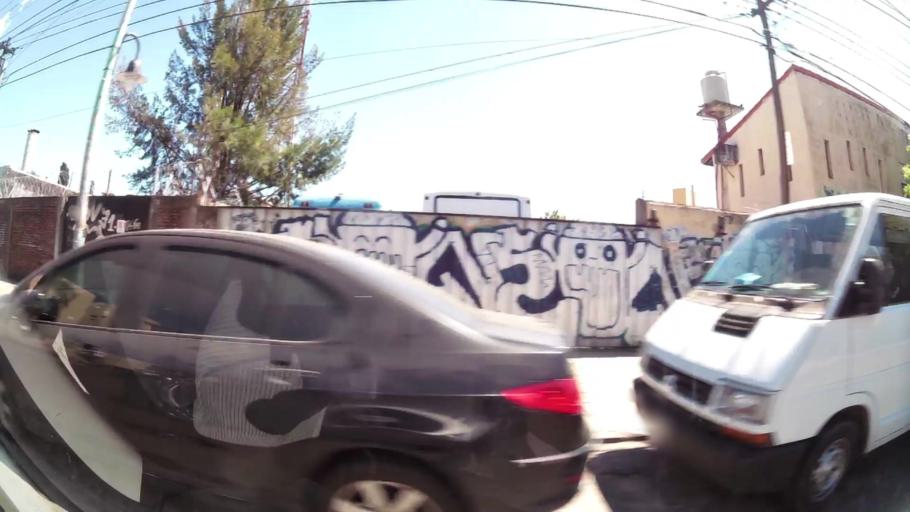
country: AR
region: Buenos Aires
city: Hurlingham
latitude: -34.5021
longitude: -58.6431
